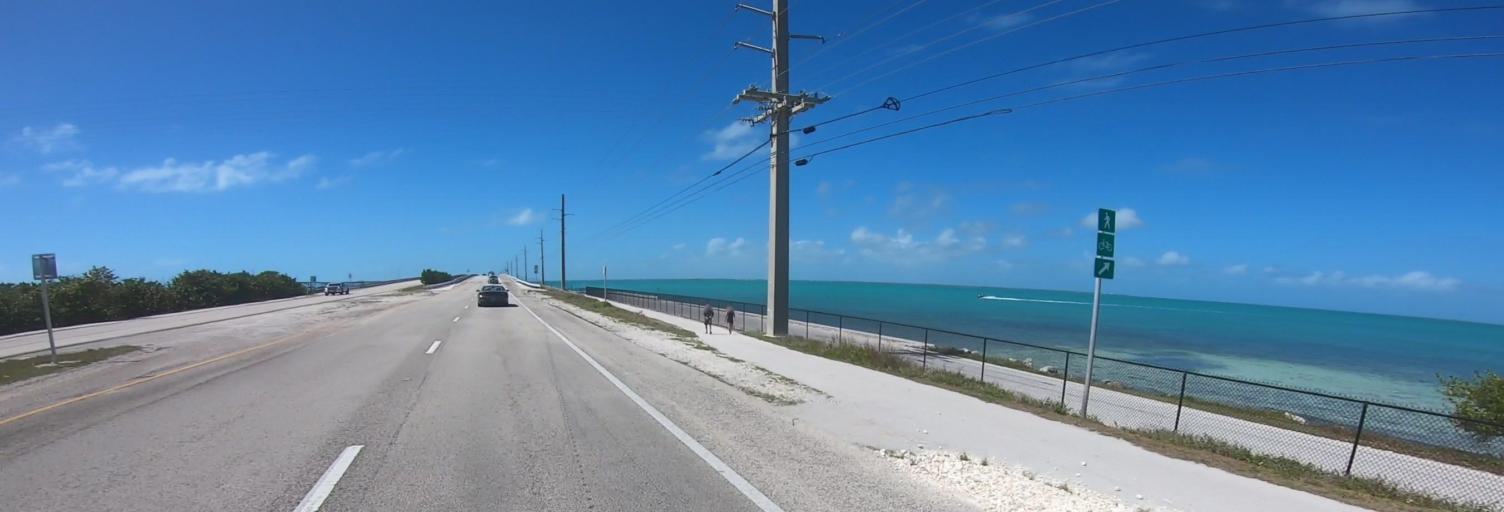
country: US
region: Florida
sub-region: Monroe County
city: Big Pine Key
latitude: 24.6600
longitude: -81.2762
